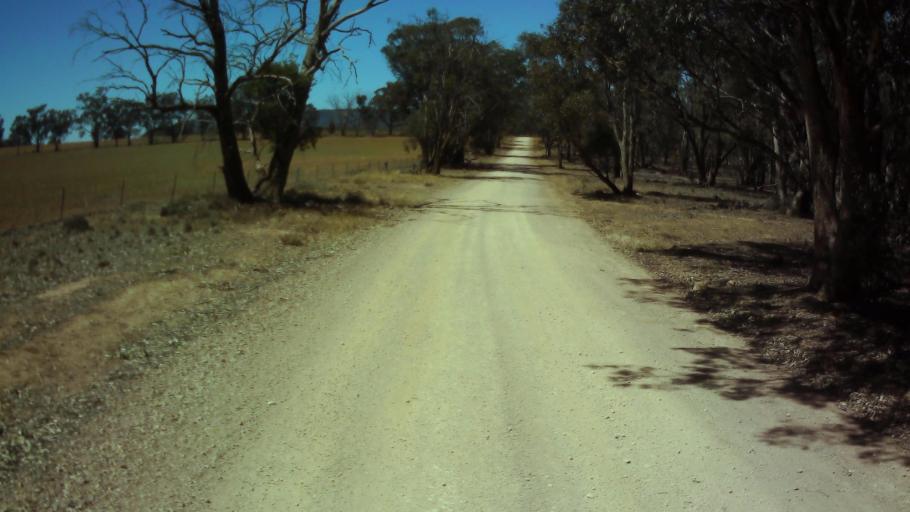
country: AU
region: New South Wales
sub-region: Weddin
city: Grenfell
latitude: -33.9289
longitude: 148.0780
